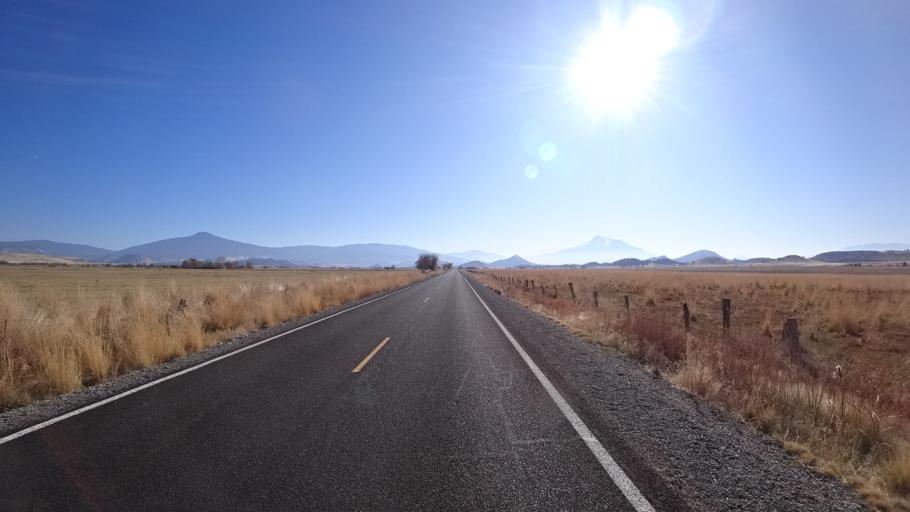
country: US
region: California
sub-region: Siskiyou County
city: Montague
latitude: 41.7168
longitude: -122.4464
